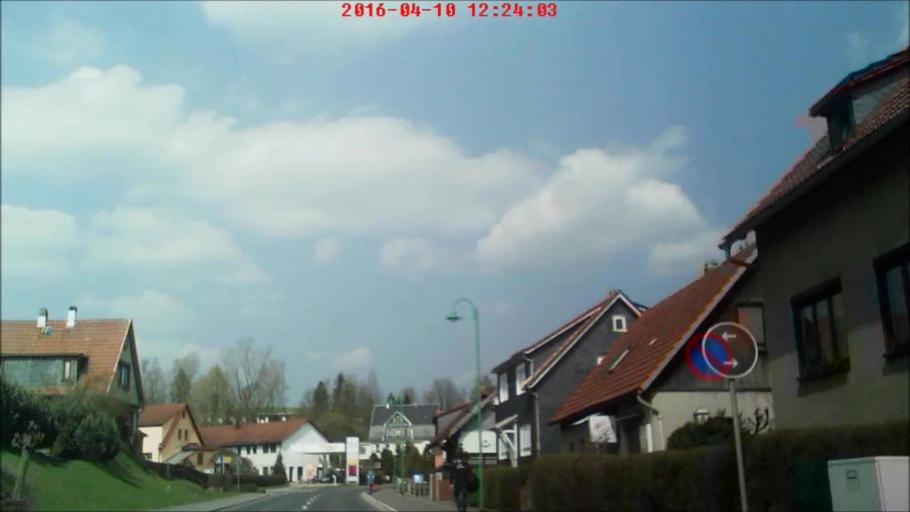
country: DE
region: Thuringia
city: Viernau
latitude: 50.6677
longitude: 10.5526
